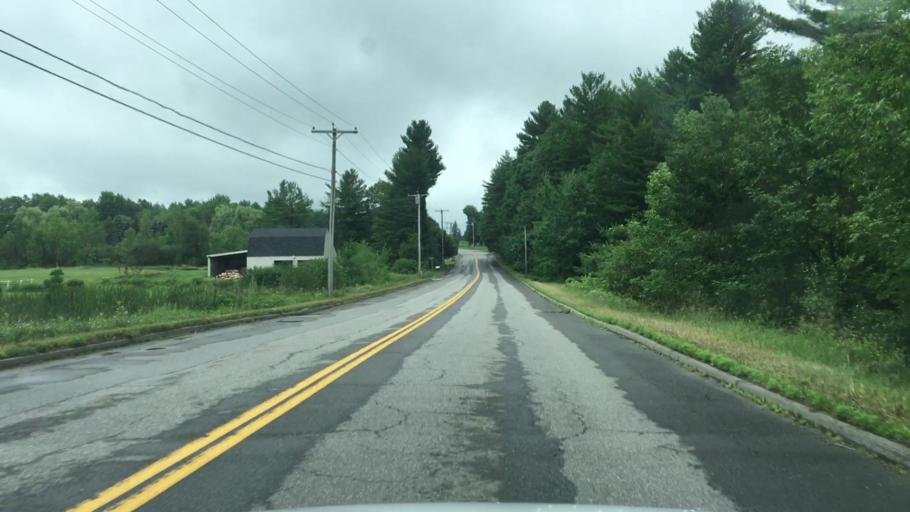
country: US
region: Maine
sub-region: Kennebec County
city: Augusta
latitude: 44.3120
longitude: -69.7398
